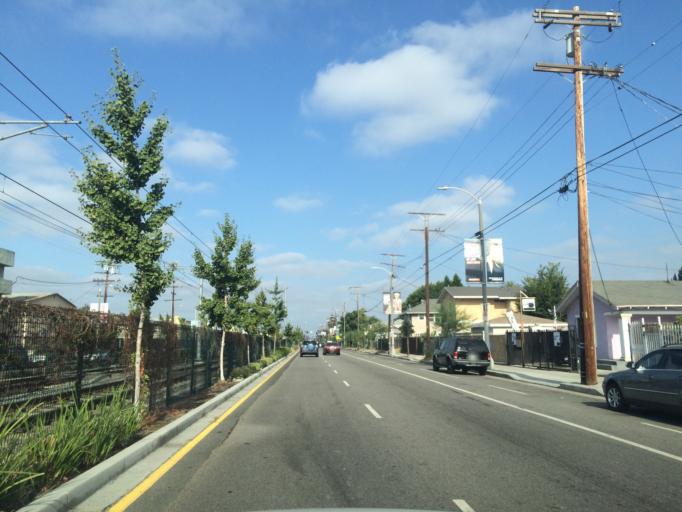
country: US
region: California
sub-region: Los Angeles County
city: View Park-Windsor Hills
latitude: 34.0183
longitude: -118.2945
